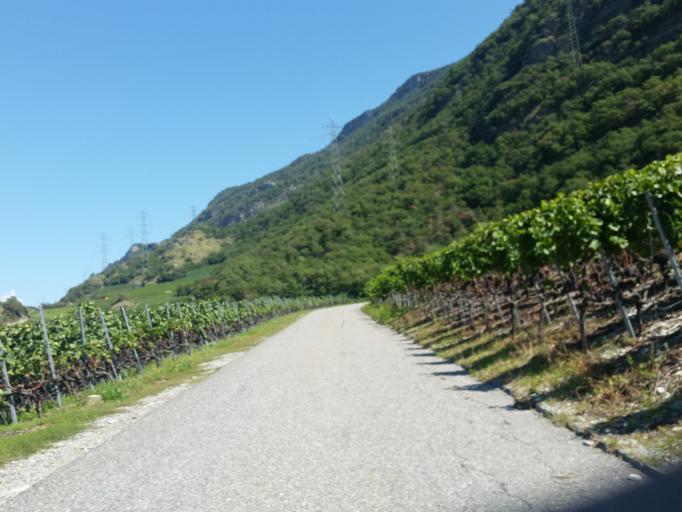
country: CH
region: Valais
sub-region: Martigny District
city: Charrat-les-Chenes
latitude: 46.1226
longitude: 7.1386
